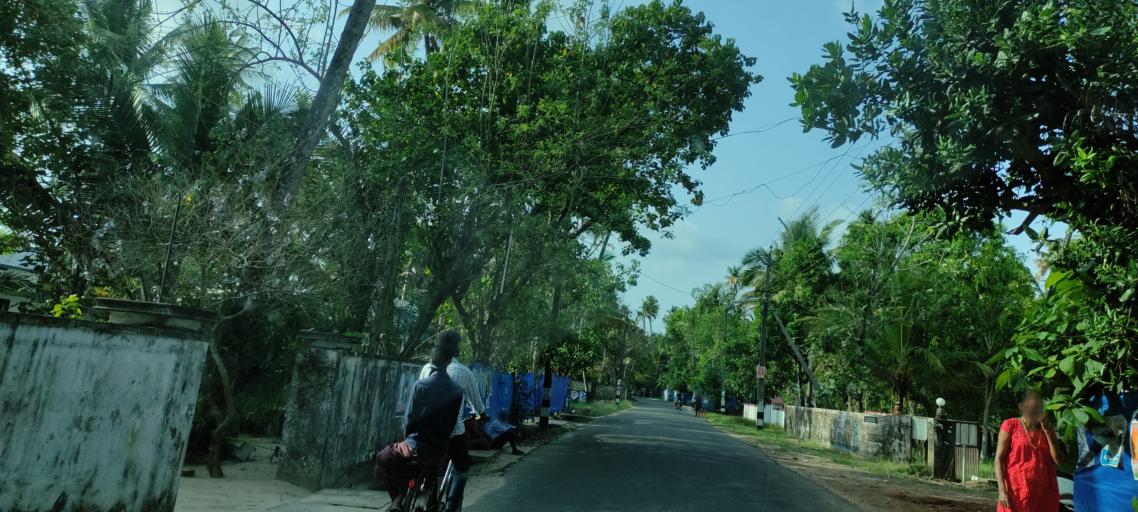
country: IN
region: Kerala
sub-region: Alappuzha
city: Vayalar
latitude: 9.7231
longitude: 76.2871
